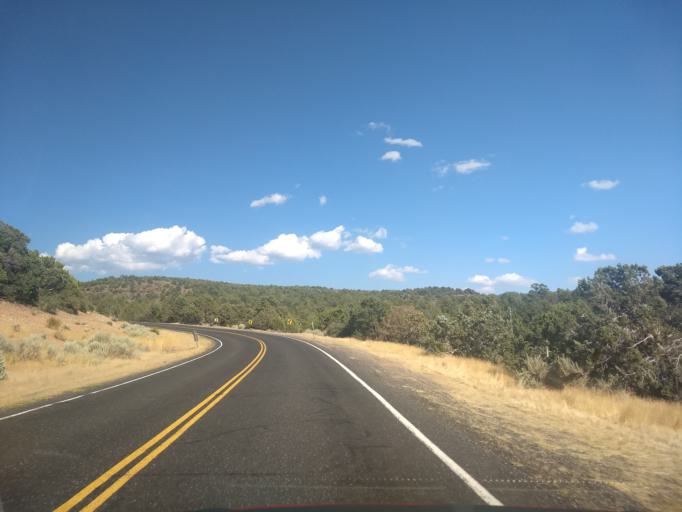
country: US
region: Utah
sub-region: Washington County
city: Enterprise
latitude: 37.4165
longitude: -113.6011
